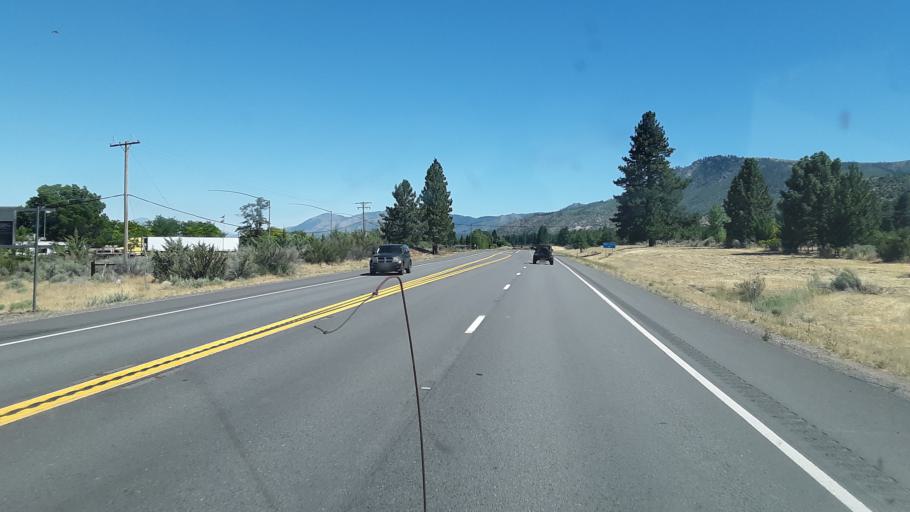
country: US
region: California
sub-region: Lassen County
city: Janesville
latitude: 40.2576
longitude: -120.4674
